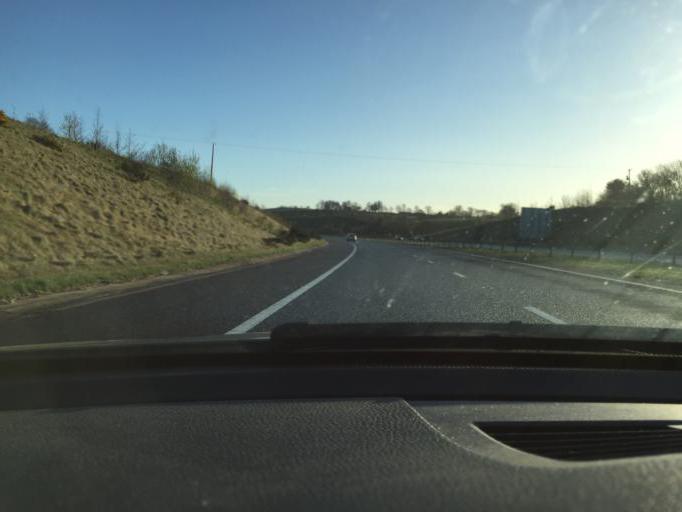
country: GB
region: Northern Ireland
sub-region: Newry and Mourne District
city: Newry
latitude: 54.2181
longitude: -6.3258
